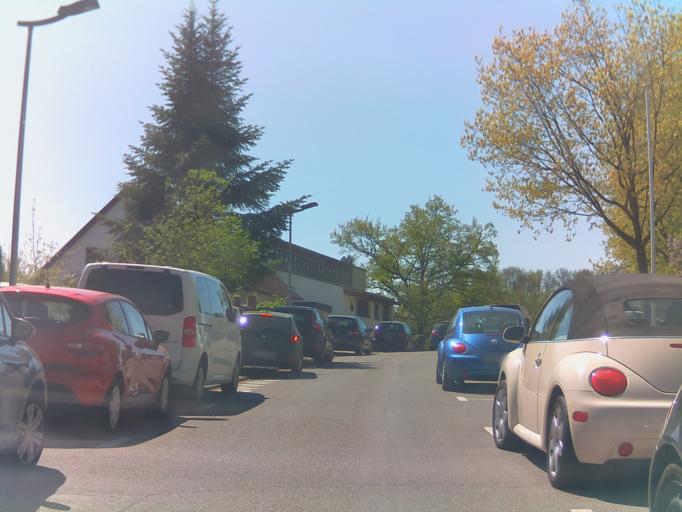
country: DE
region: Baden-Wuerttemberg
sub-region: Freiburg Region
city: Rottweil
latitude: 48.1611
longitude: 8.6261
